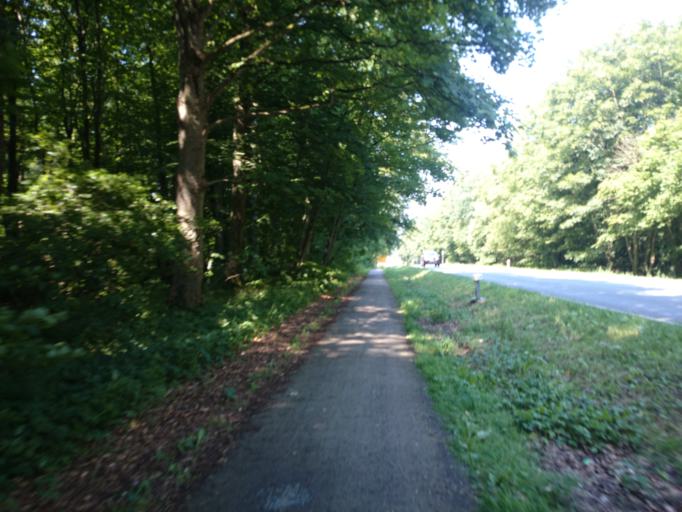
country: DE
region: Mecklenburg-Vorpommern
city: Broderstorf
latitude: 54.0772
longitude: 12.3047
